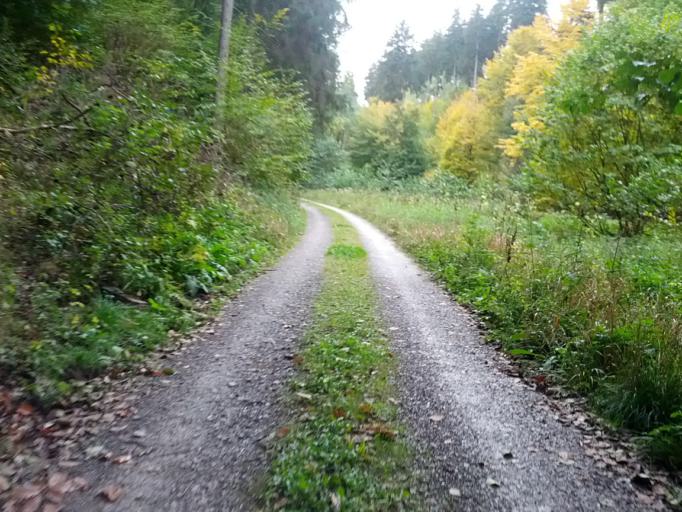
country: DE
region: Thuringia
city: Krauthausen
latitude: 50.9794
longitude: 10.2764
